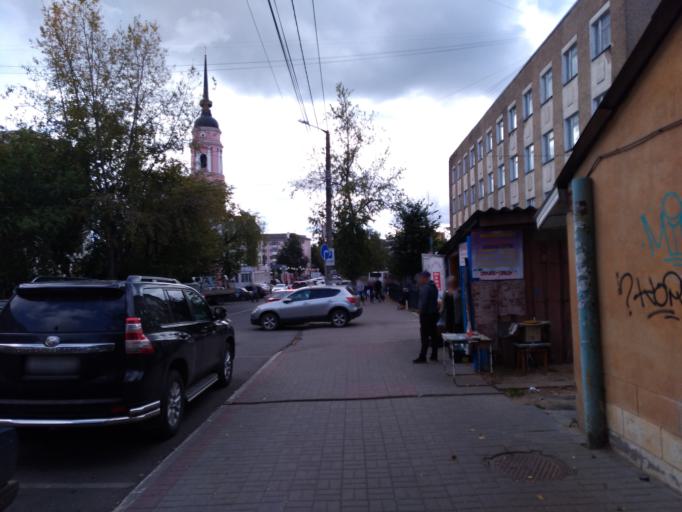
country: RU
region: Kaluga
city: Kaluga
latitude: 54.5164
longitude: 36.2542
